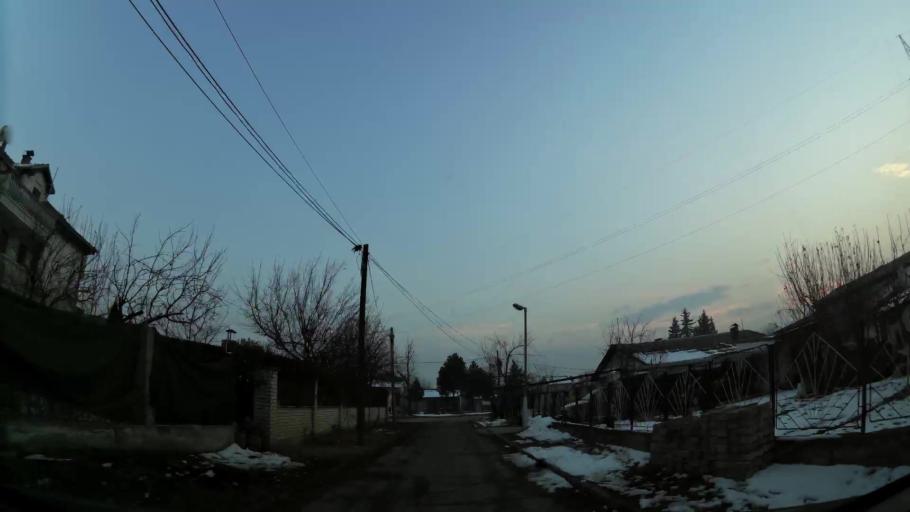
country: MK
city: Creshevo
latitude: 42.0052
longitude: 21.5077
